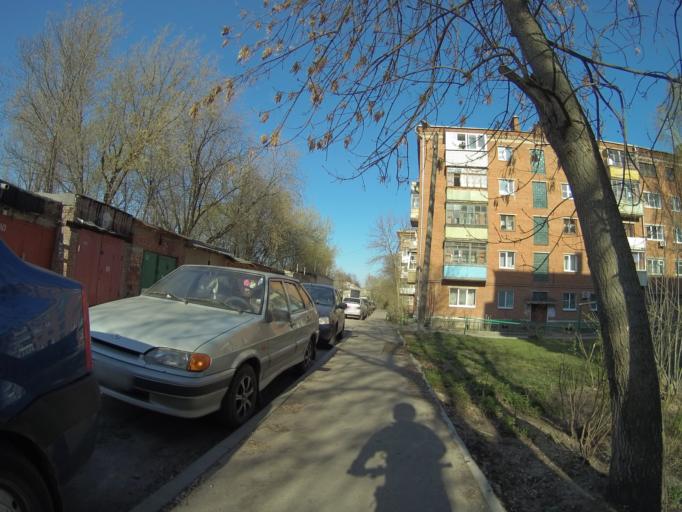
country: RU
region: Vladimir
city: Vladimir
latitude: 56.1509
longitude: 40.4204
